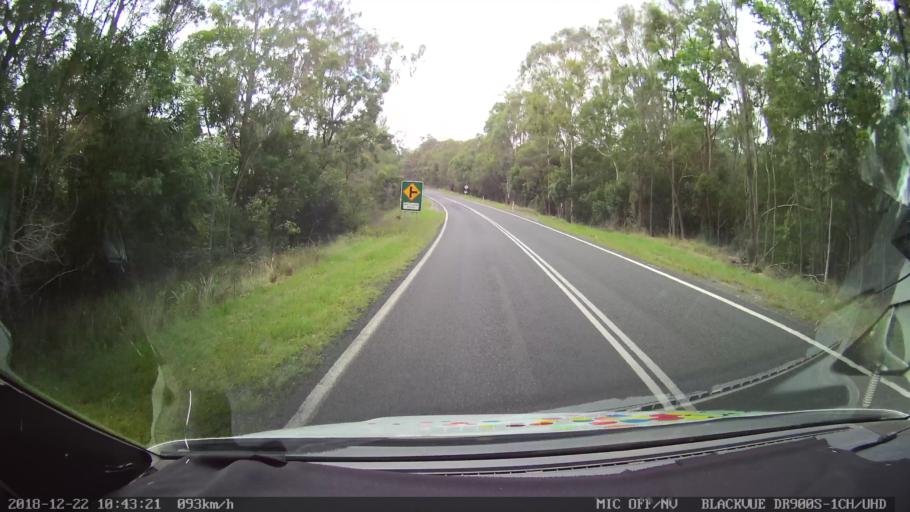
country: AU
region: New South Wales
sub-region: Clarence Valley
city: South Grafton
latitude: -29.6447
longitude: 152.7872
